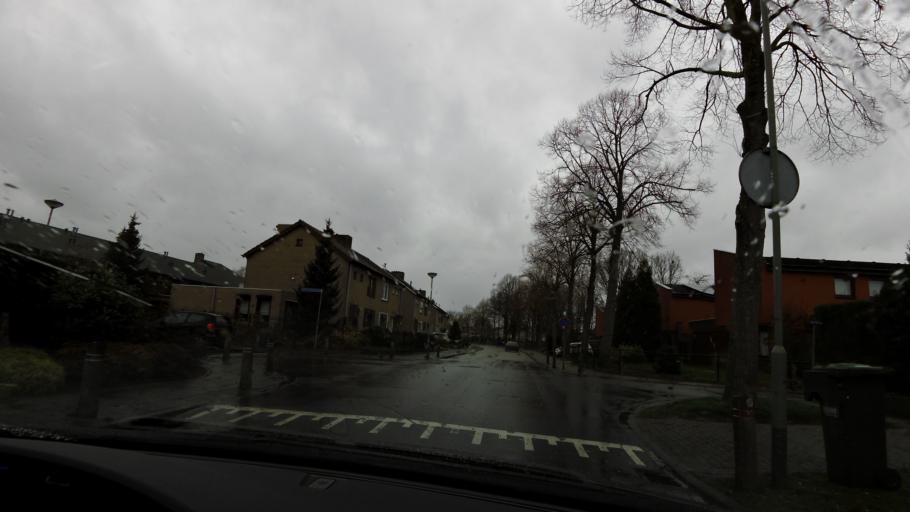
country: NL
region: Limburg
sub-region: Gemeente Stein
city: Elsloo
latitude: 50.9516
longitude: 5.7767
